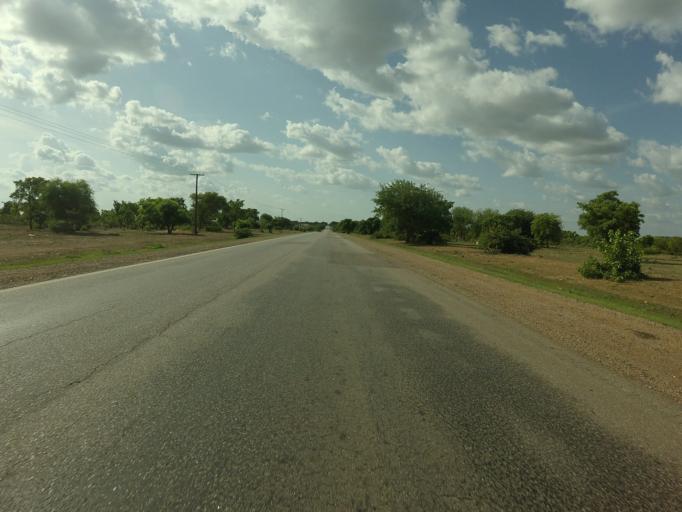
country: GH
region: Upper East
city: Bolgatanga
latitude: 10.6522
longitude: -0.8581
